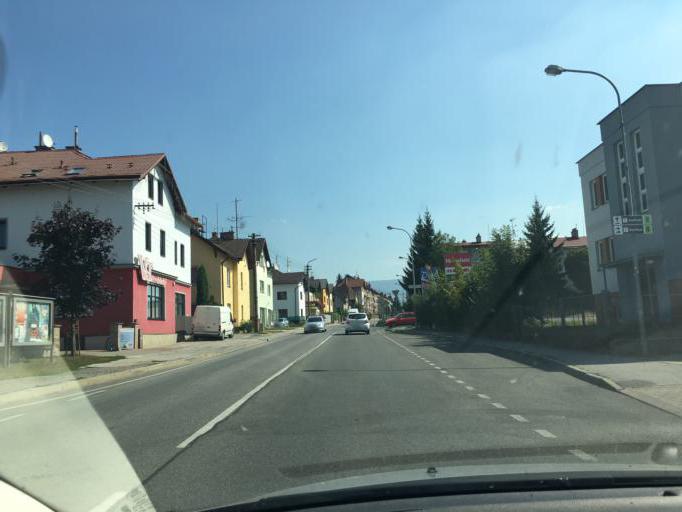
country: CZ
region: Kralovehradecky
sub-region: Okres Trutnov
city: Vrchlabi
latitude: 50.6206
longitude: 15.6207
